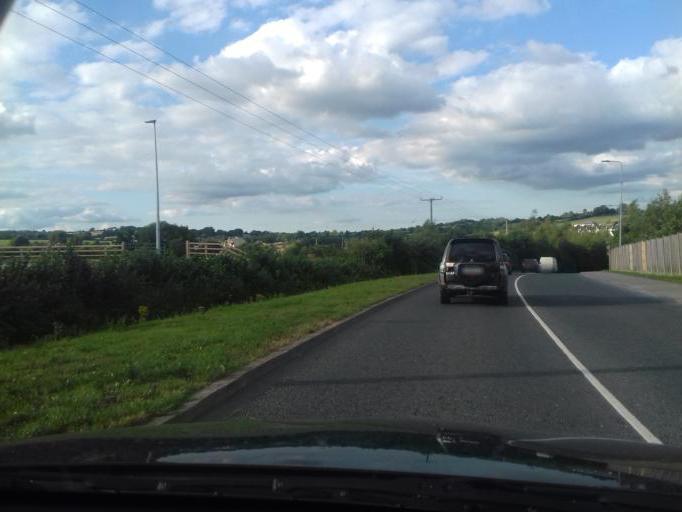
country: IE
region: Leinster
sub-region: Kilkenny
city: Graiguenamanagh
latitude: 52.5411
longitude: -6.9634
